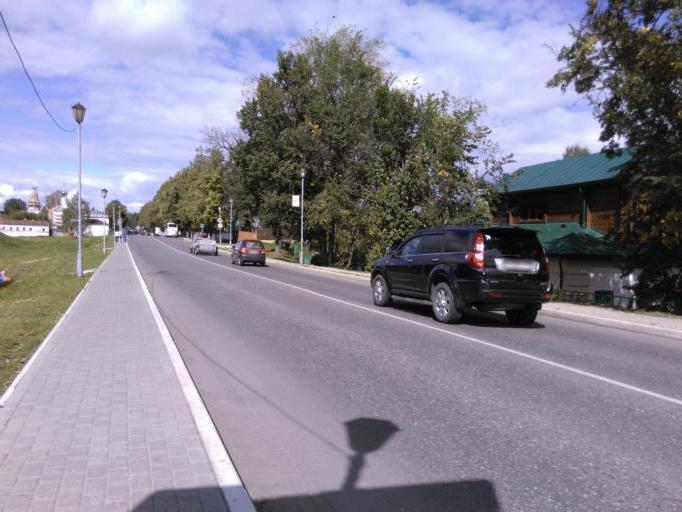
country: RU
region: Vladimir
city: Suzdal'
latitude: 56.4143
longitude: 40.4479
